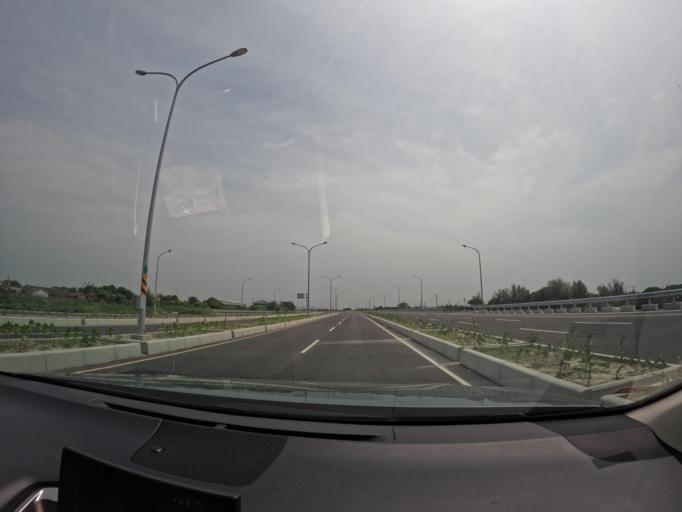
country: TW
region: Taiwan
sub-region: Changhua
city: Chang-hua
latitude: 23.9374
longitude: 120.3262
